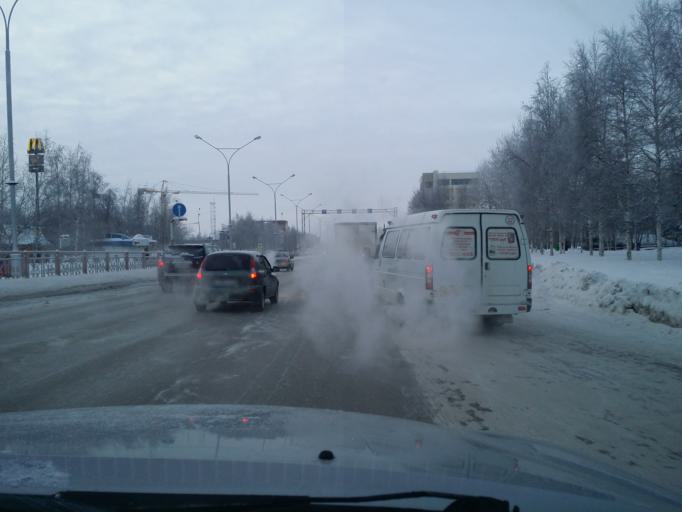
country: RU
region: Khanty-Mansiyskiy Avtonomnyy Okrug
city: Nizhnevartovsk
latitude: 60.9397
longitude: 76.5627
